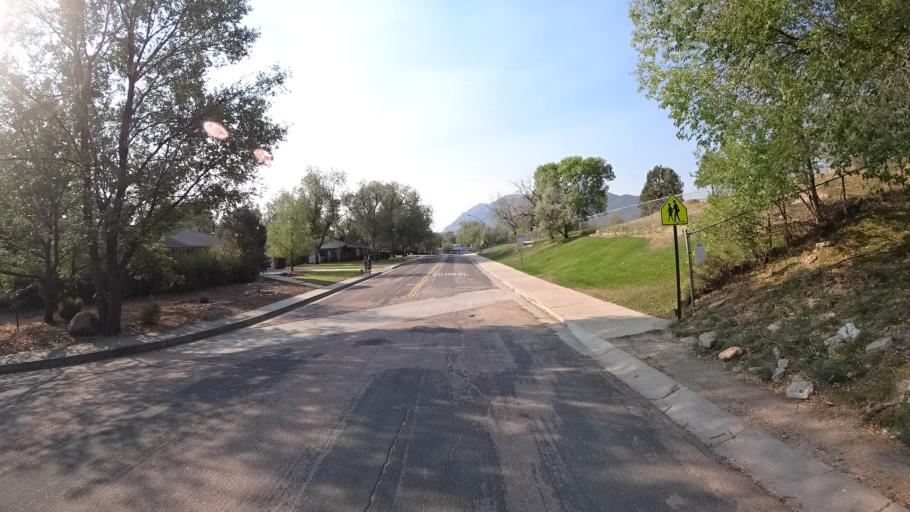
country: US
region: Colorado
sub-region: El Paso County
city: Colorado Springs
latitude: 38.8074
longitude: -104.8488
